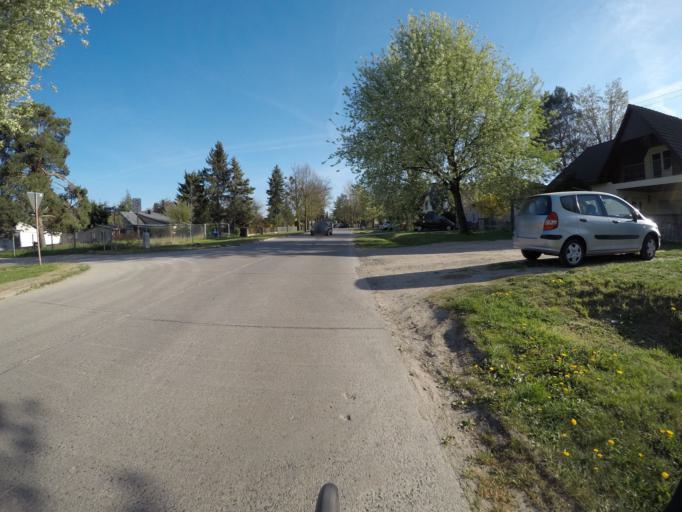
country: DE
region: Brandenburg
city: Neuenhagen
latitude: 52.5142
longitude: 13.7232
